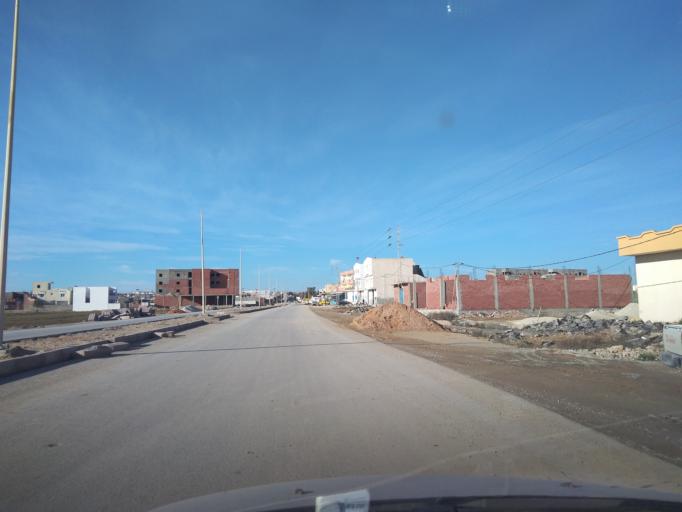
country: TN
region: Ariana
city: Qal'at al Andalus
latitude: 37.0502
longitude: 10.1235
